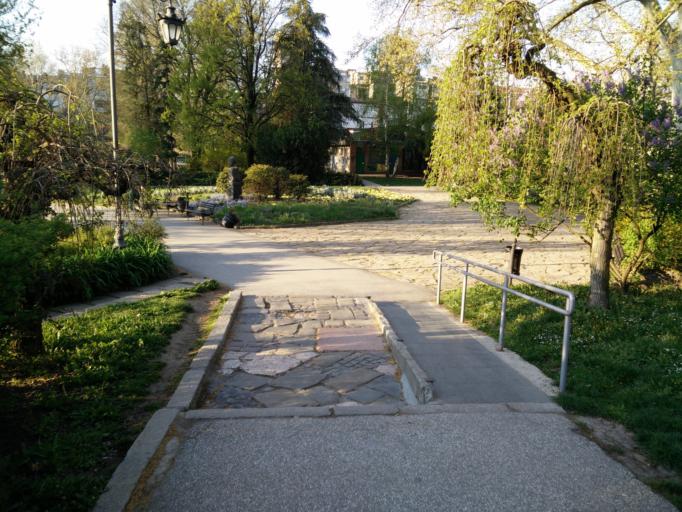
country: RS
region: Autonomna Pokrajina Vojvodina
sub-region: Juznobacki Okrug
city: Novi Sad
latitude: 45.2556
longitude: 19.8503
